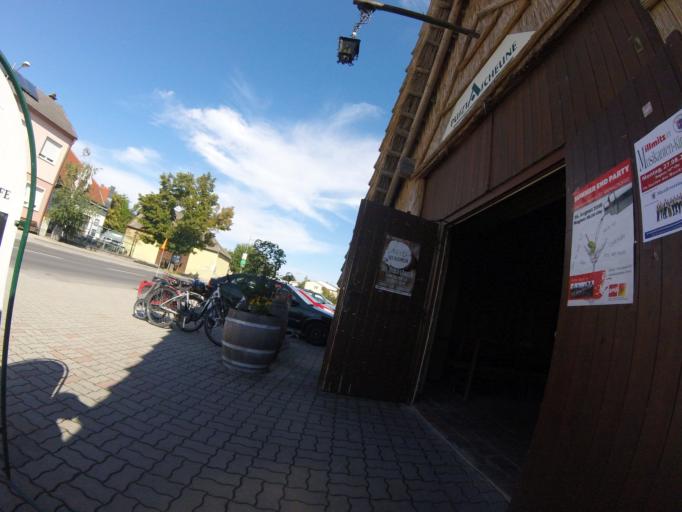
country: AT
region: Burgenland
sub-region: Politischer Bezirk Neusiedl am See
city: Illmitz
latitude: 47.7621
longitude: 16.8021
